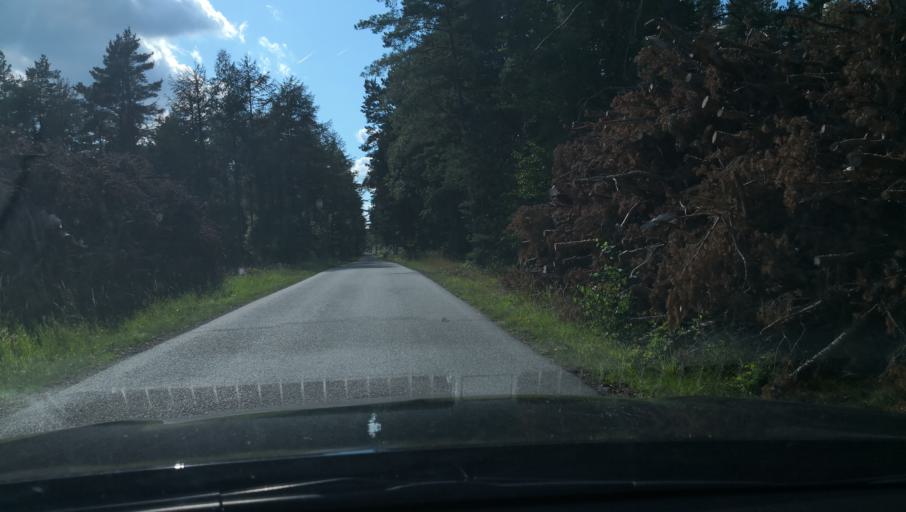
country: SE
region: Skane
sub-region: Simrishamns Kommun
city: Kivik
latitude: 55.7685
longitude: 14.1816
